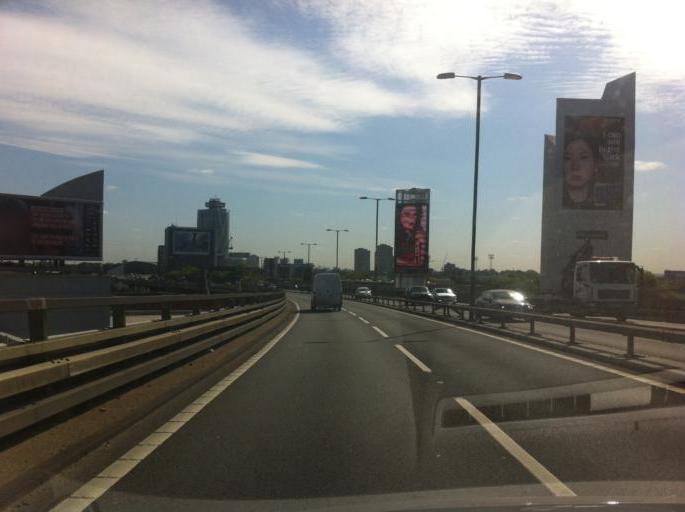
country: GB
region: England
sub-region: Greater London
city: Brentford
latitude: 51.4888
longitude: -0.3145
